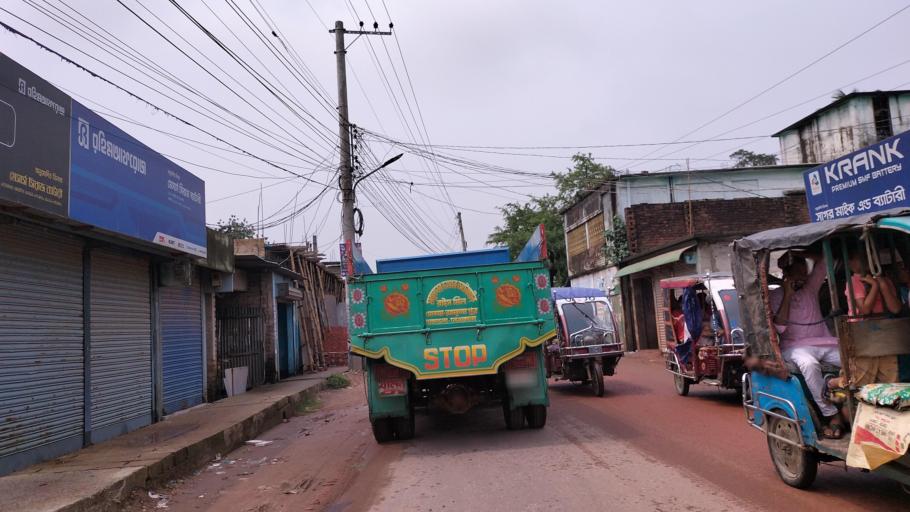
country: BD
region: Dhaka
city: Netrakona
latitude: 24.8884
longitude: 90.7382
